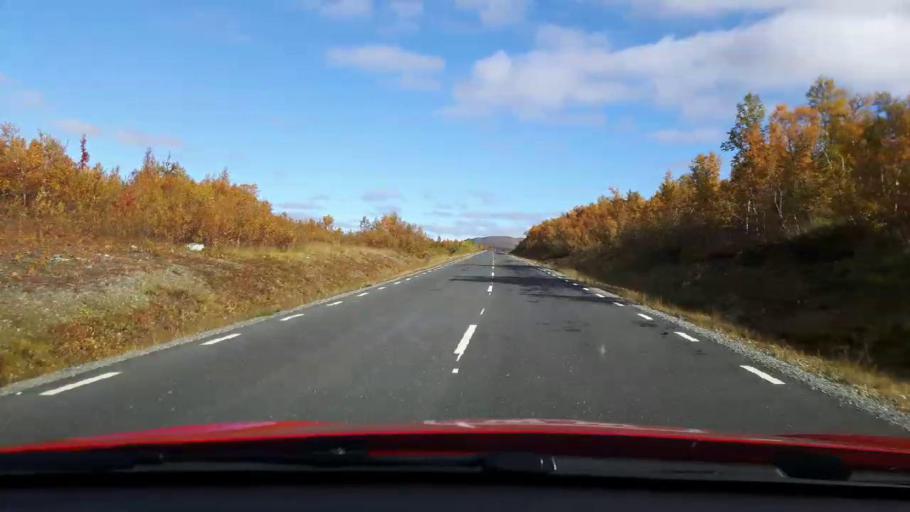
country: NO
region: Nordland
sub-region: Hattfjelldal
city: Hattfjelldal
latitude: 65.0025
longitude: 14.2505
